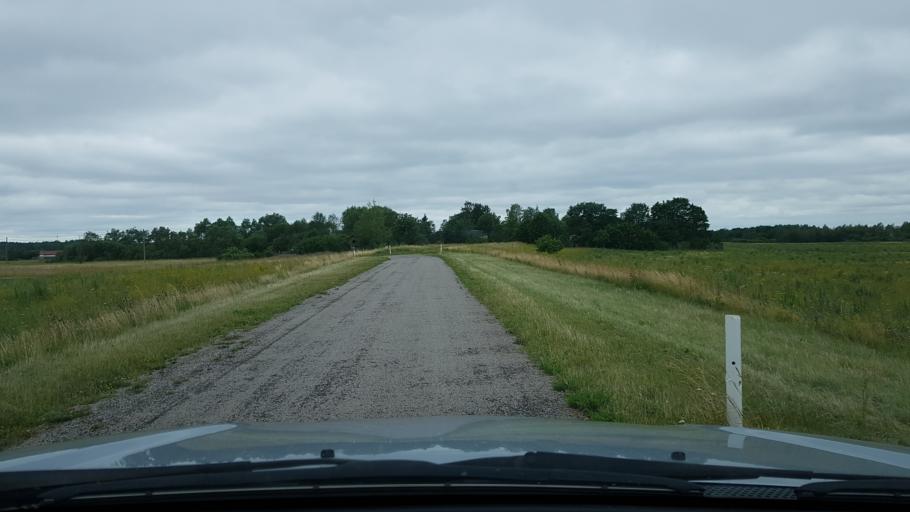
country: EE
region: Ida-Virumaa
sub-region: Narva linn
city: Narva
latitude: 59.3849
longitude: 28.1406
